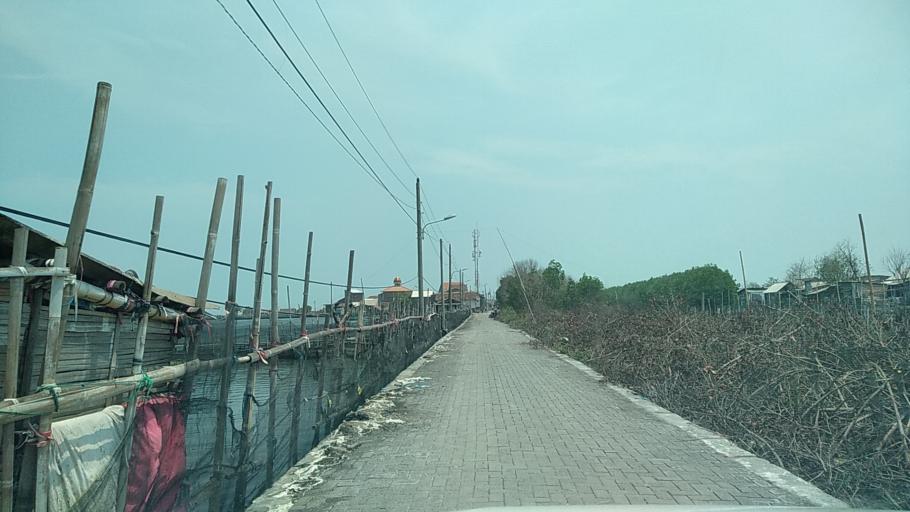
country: ID
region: Central Java
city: Semarang
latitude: -6.9494
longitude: 110.4403
